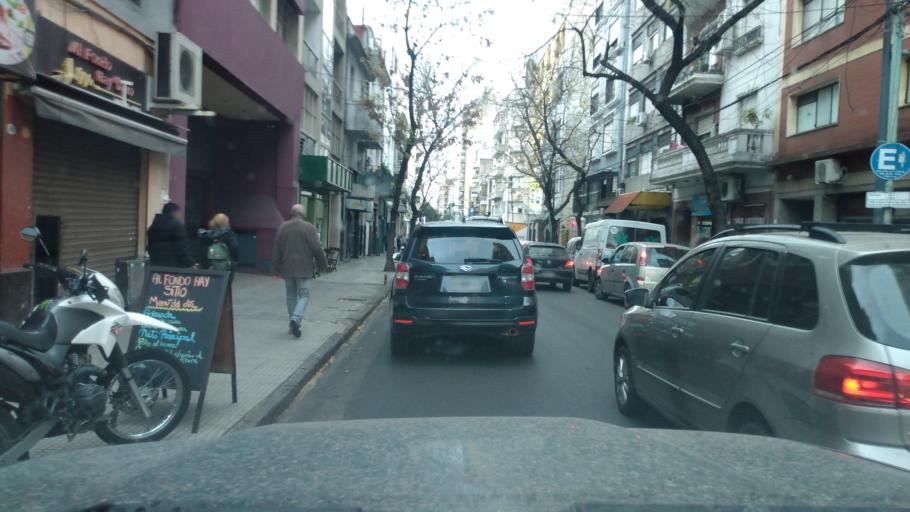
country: AR
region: Buenos Aires F.D.
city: Buenos Aires
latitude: -34.6025
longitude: -58.3970
